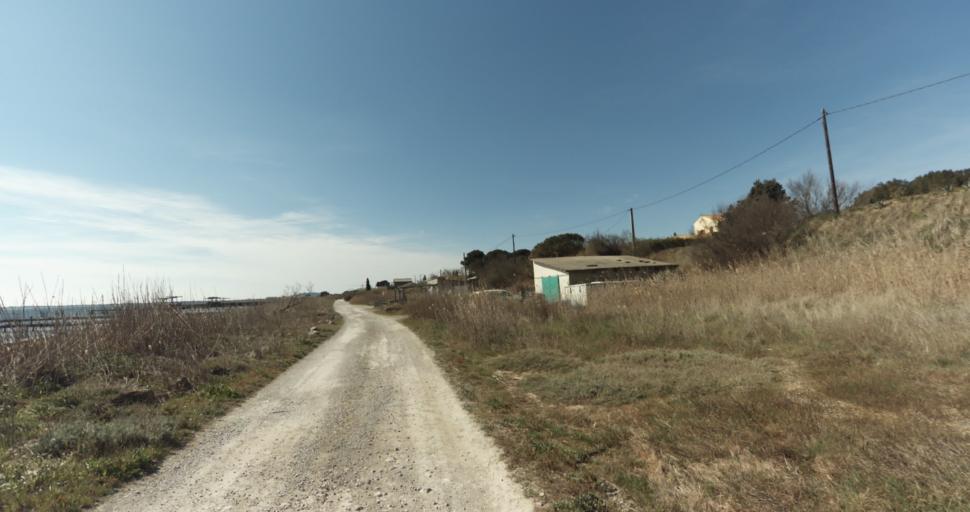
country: FR
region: Languedoc-Roussillon
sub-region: Departement de l'Herault
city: Marseillan
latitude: 43.3702
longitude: 3.5417
